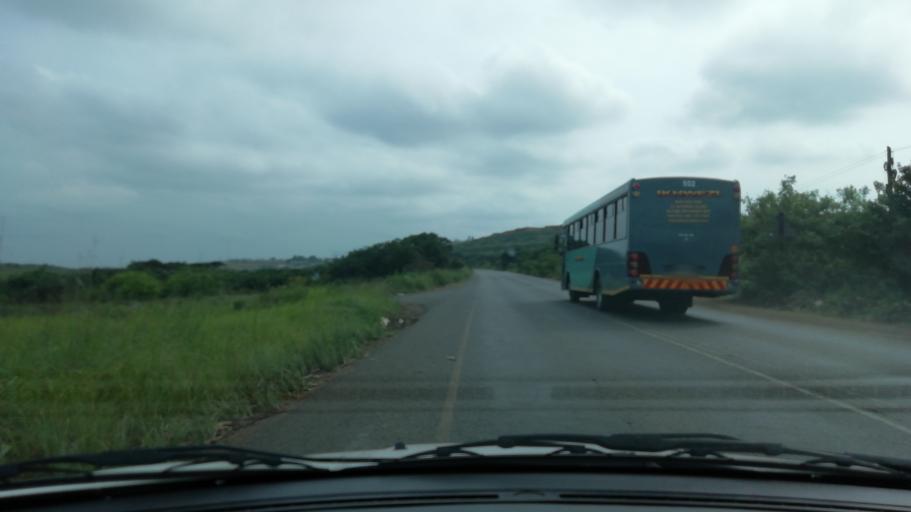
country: ZA
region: KwaZulu-Natal
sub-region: uThungulu District Municipality
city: Empangeni
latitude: -28.7500
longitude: 31.8791
